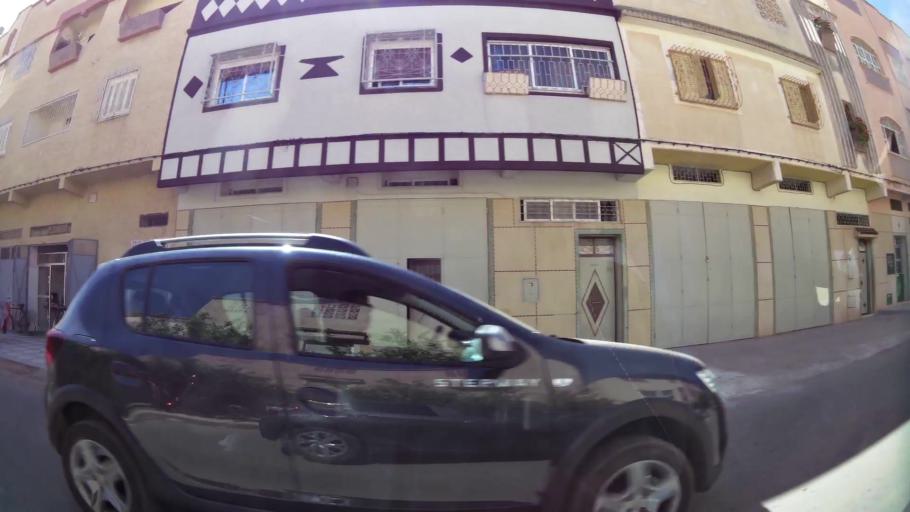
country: MA
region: Oriental
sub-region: Oujda-Angad
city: Oujda
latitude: 34.6670
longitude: -1.9330
